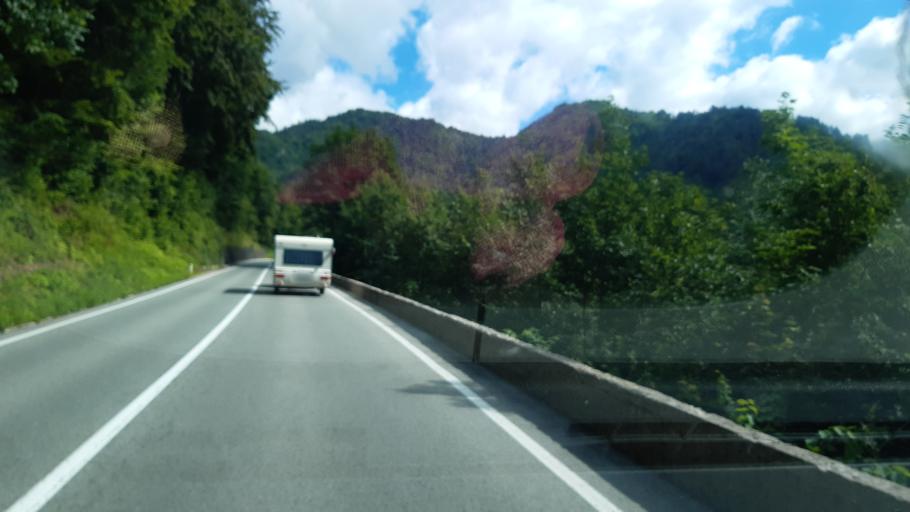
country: SI
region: Trzic
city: Trzic
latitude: 46.3636
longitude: 14.3055
